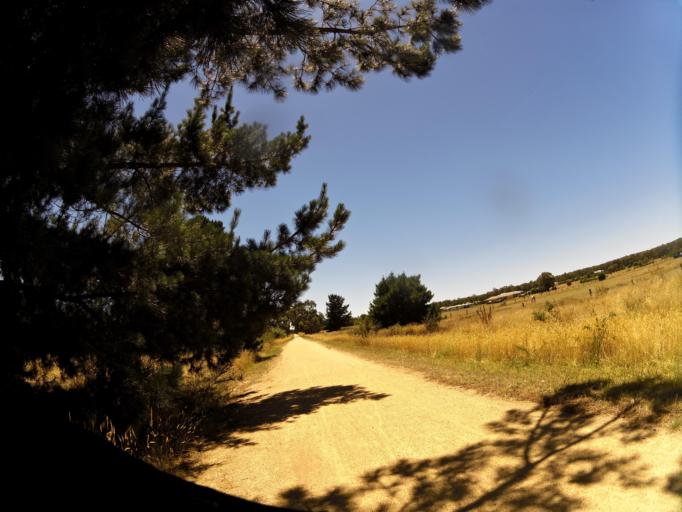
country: AU
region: Victoria
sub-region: Ballarat North
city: Delacombe
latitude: -37.5976
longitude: 143.7190
